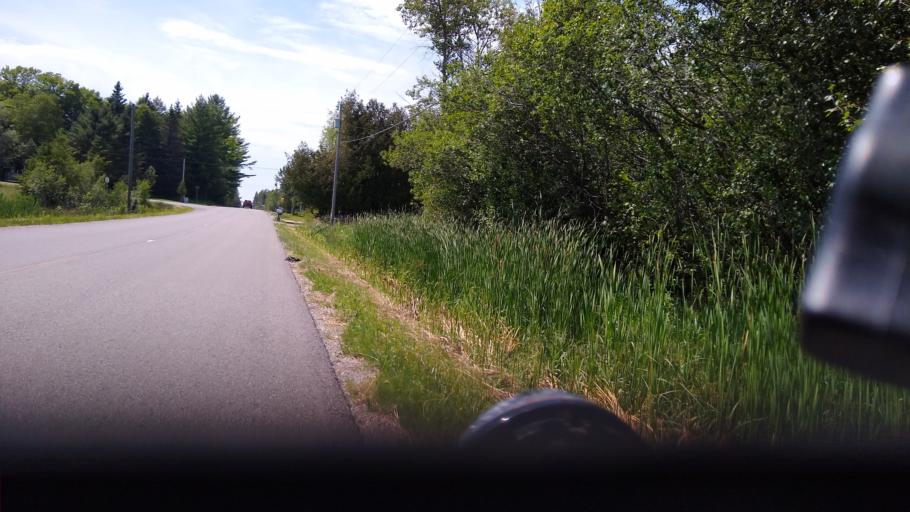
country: US
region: Michigan
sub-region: Delta County
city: Escanaba
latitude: 45.7102
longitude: -87.1201
